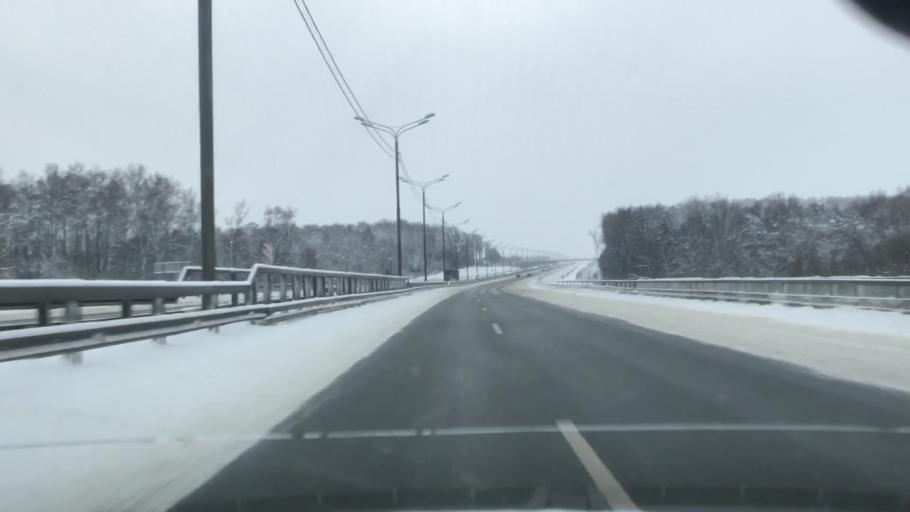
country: RU
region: Moskovskaya
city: Barybino
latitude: 55.2744
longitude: 37.8663
